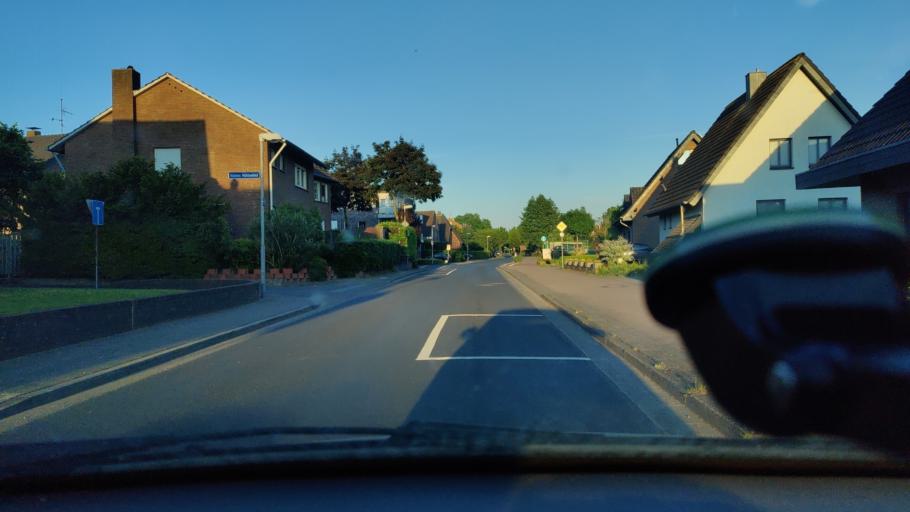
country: DE
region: North Rhine-Westphalia
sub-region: Regierungsbezirk Dusseldorf
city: Kranenburg
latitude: 51.7871
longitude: 6.0075
